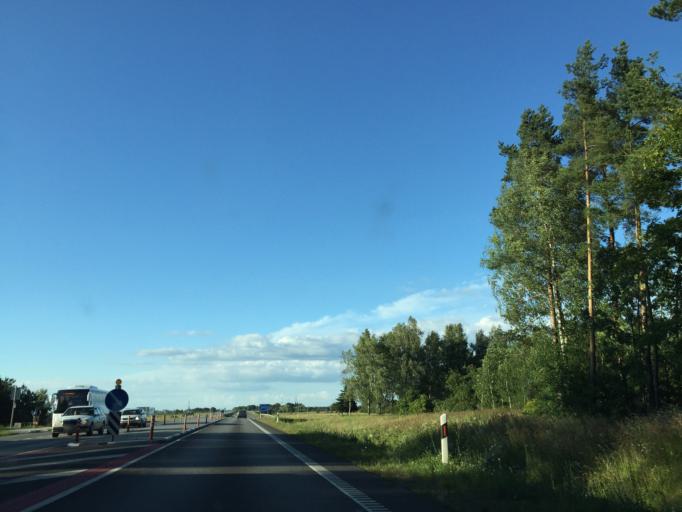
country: LT
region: Panevezys
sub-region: Panevezys City
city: Panevezys
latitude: 55.6560
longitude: 24.3582
